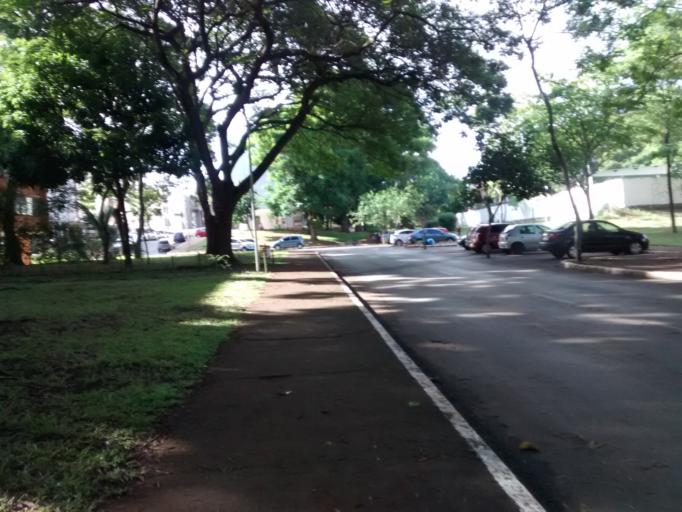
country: BR
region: Federal District
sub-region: Brasilia
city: Brasilia
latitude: -15.7517
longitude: -47.8821
